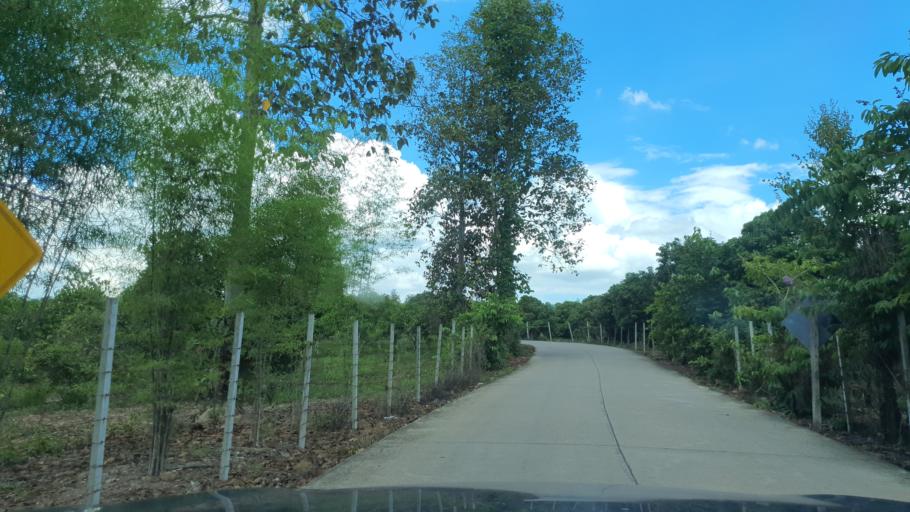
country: TH
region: Chiang Mai
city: San Sai
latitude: 18.9228
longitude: 99.0406
